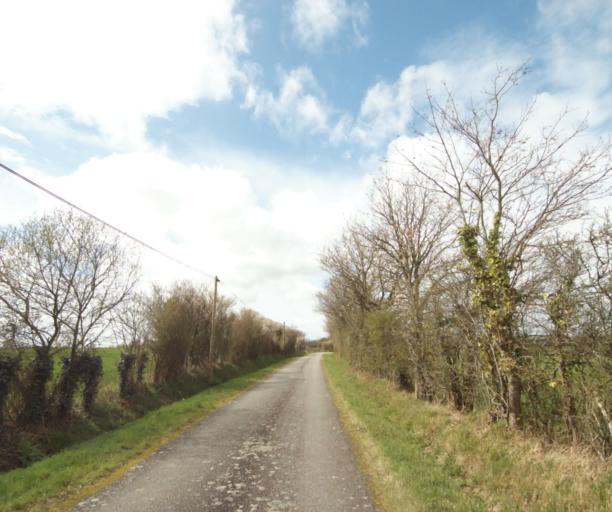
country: FR
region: Pays de la Loire
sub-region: Departement de la Loire-Atlantique
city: Bouvron
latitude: 47.4281
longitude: -1.8691
